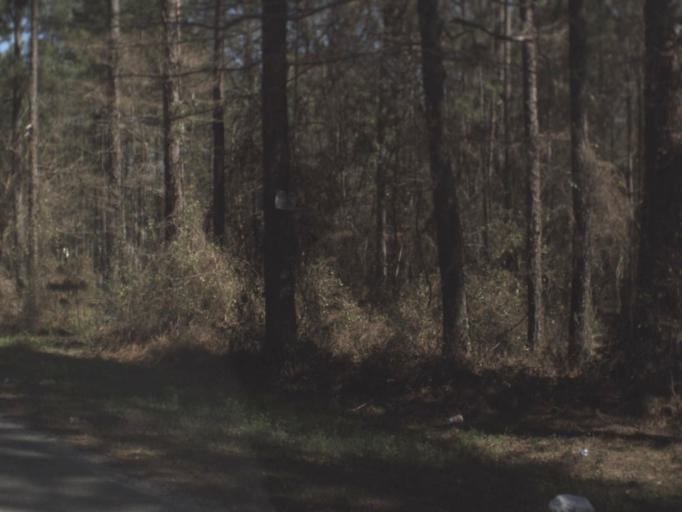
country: US
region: Florida
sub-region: Leon County
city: Woodville
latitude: 30.3179
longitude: -84.3116
